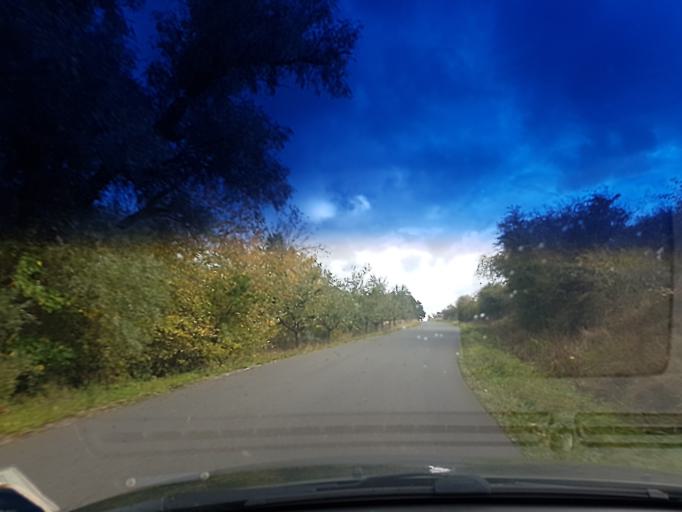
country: DE
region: Bavaria
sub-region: Regierungsbezirk Mittelfranken
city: Burghaslach
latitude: 49.7580
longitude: 10.5719
